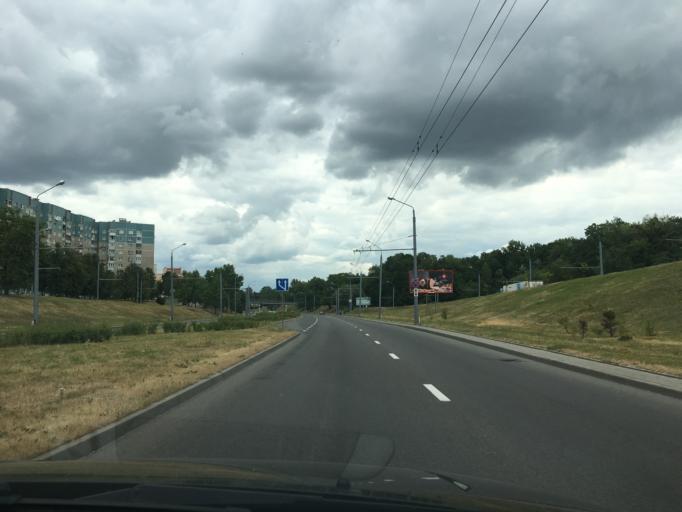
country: BY
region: Grodnenskaya
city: Hrodna
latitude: 53.6527
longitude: 23.8544
